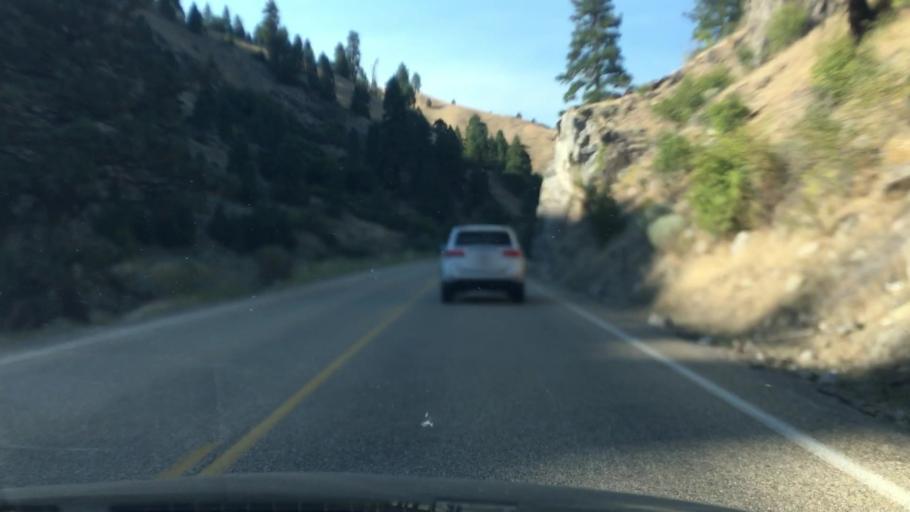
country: US
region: Idaho
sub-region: Boise County
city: Idaho City
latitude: 44.0933
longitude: -116.1023
